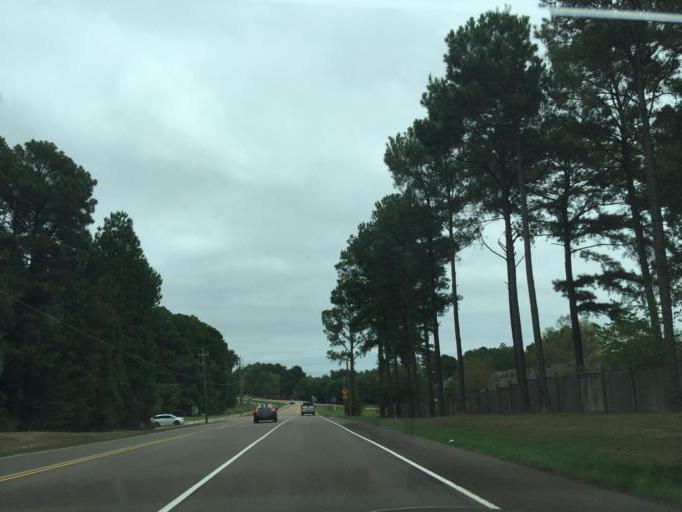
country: US
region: Mississippi
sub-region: Madison County
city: Madison
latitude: 32.4065
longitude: -90.0096
